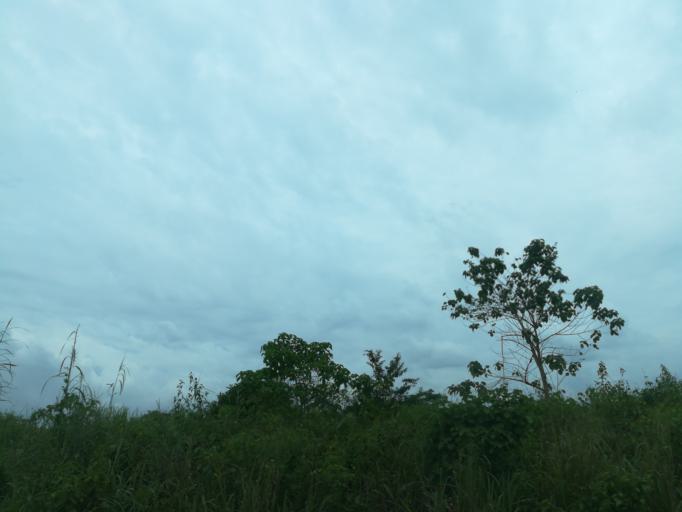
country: NG
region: Lagos
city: Ejirin
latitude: 6.6569
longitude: 3.8202
